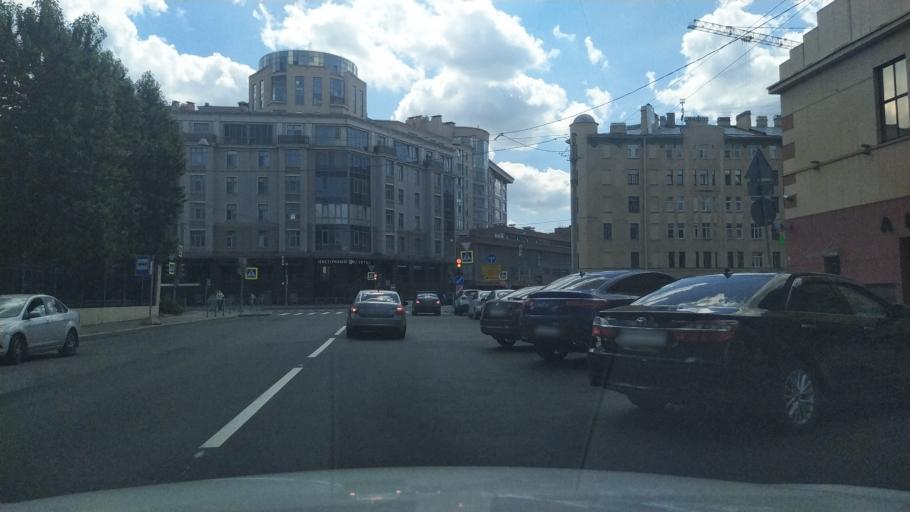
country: RU
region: St.-Petersburg
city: Novaya Derevnya
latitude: 59.9669
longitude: 30.2886
